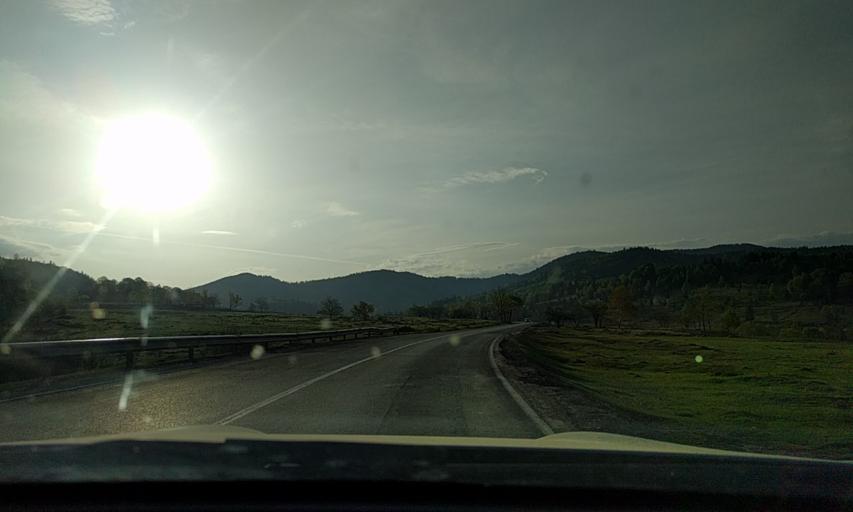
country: RO
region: Covasna
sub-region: Comuna Bretcu
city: Bretcu
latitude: 46.0449
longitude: 26.3285
